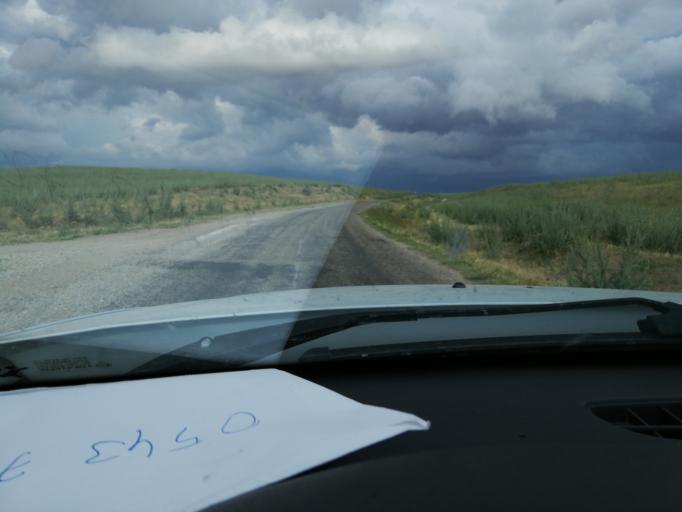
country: TR
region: Kirsehir
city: Kirsehir
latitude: 39.0432
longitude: 34.1652
